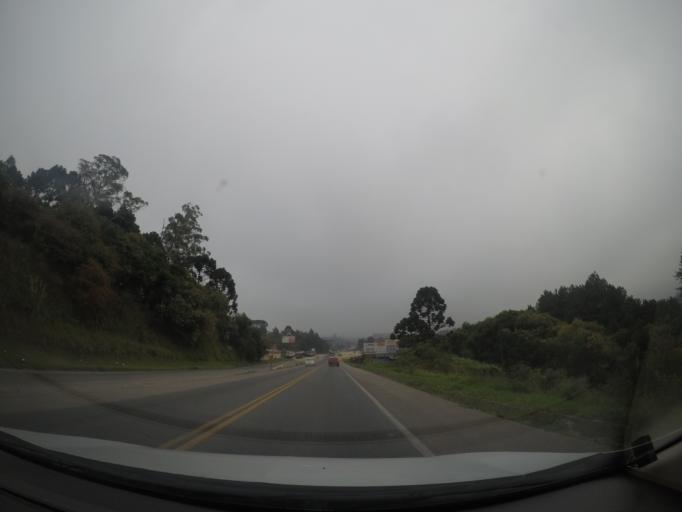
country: BR
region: Parana
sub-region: Almirante Tamandare
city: Almirante Tamandare
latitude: -25.3243
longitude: -49.2973
